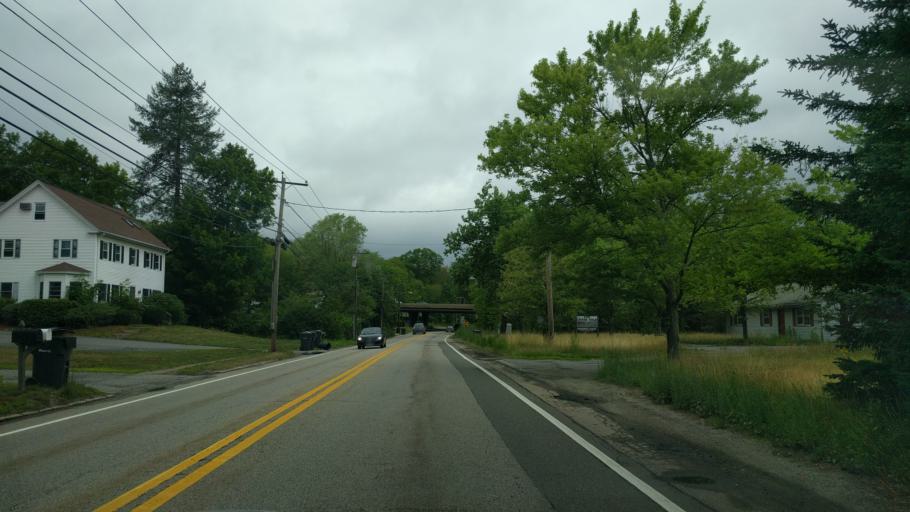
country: US
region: Massachusetts
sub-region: Worcester County
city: Grafton
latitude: 42.2237
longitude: -71.7047
